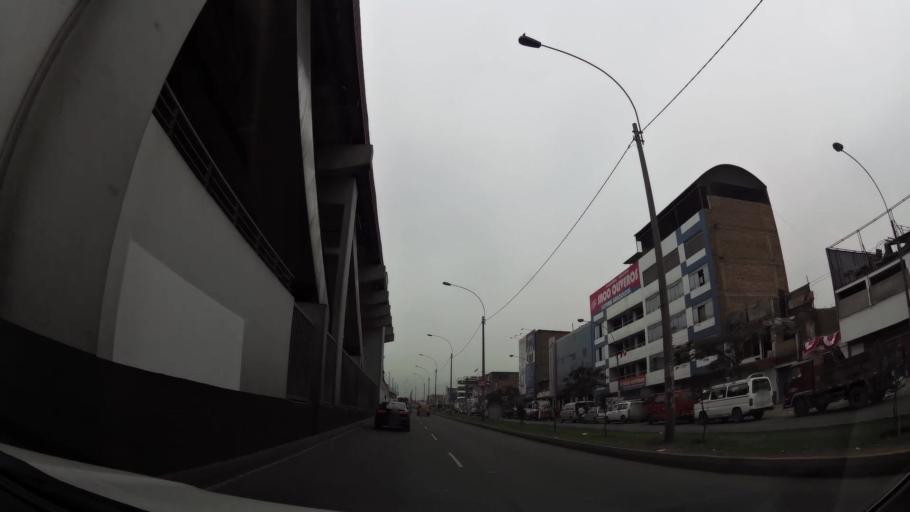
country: PE
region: Lima
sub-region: Lima
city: Independencia
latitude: -11.9746
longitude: -76.9998
